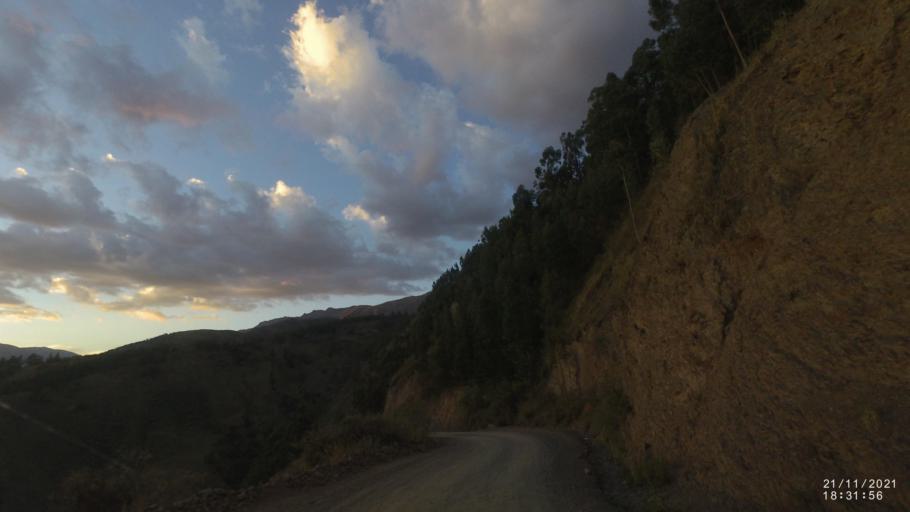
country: BO
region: Cochabamba
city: Cochabamba
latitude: -17.3107
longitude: -66.2169
